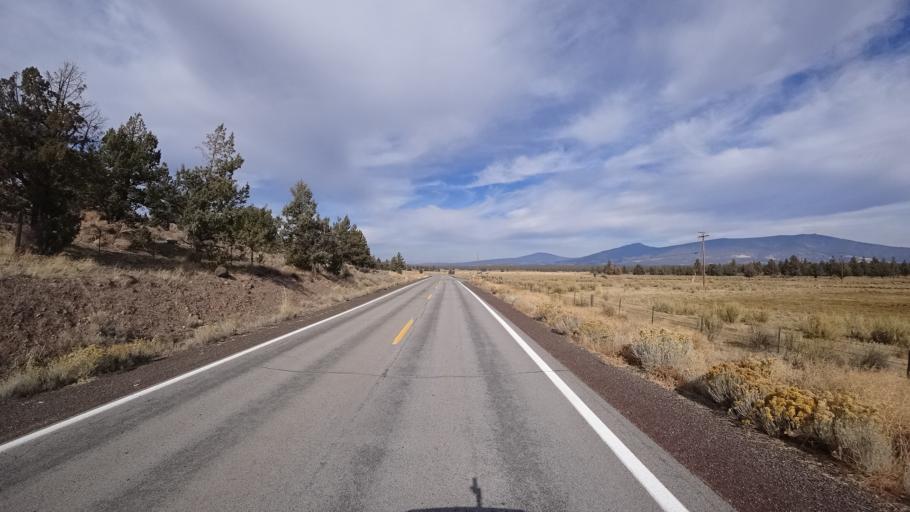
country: US
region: California
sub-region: Siskiyou County
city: Weed
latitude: 41.5635
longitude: -122.3868
